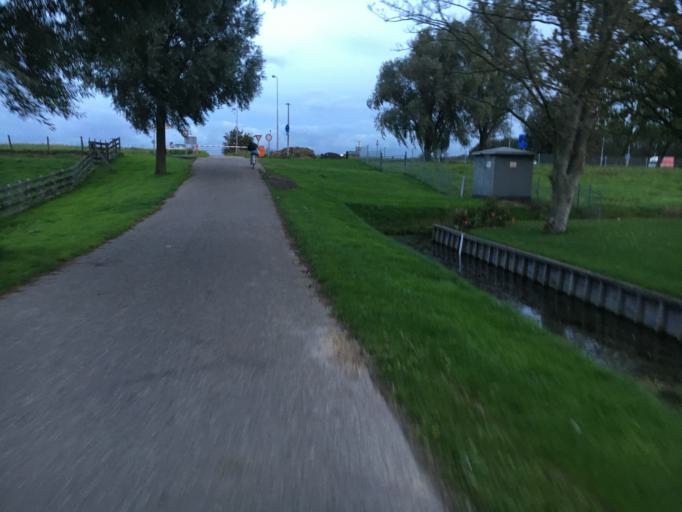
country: NL
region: North Holland
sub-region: Gemeente Ouder-Amstel
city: Ouderkerk aan de Amstel
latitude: 52.3053
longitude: 4.9248
